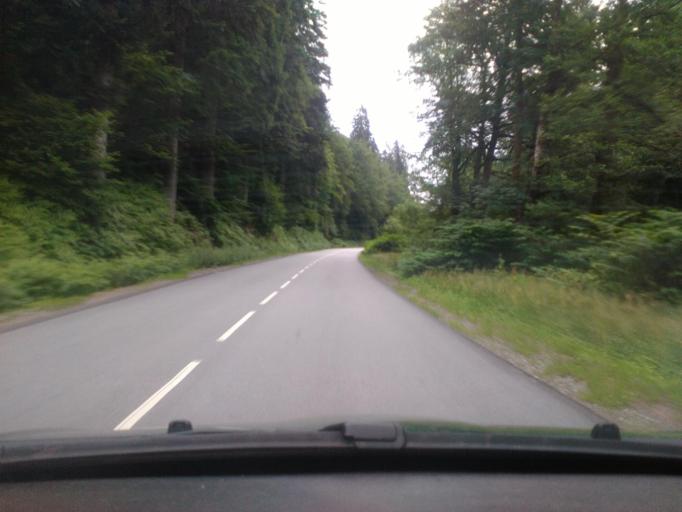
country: FR
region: Lorraine
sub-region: Departement des Vosges
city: Gerardmer
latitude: 48.1117
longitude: 6.8551
